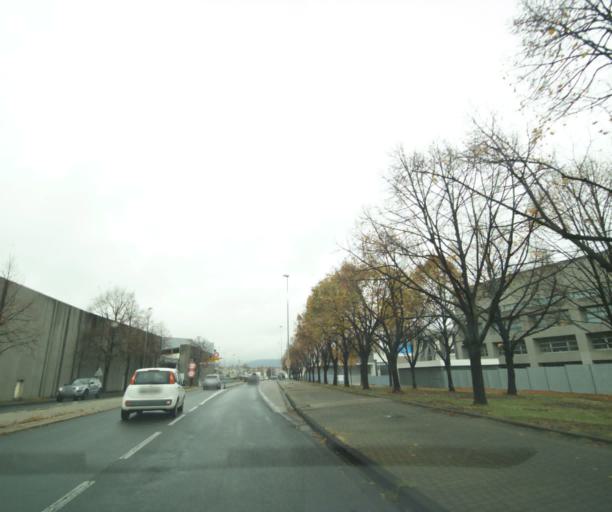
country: FR
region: Auvergne
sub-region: Departement du Puy-de-Dome
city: Aubiere
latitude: 45.7617
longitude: 3.1310
